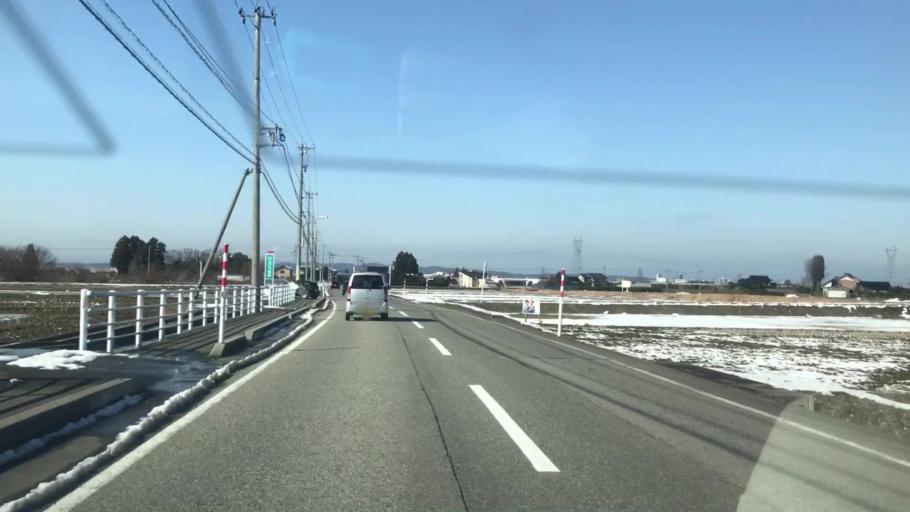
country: JP
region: Toyama
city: Toyama-shi
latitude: 36.6447
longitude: 137.2531
